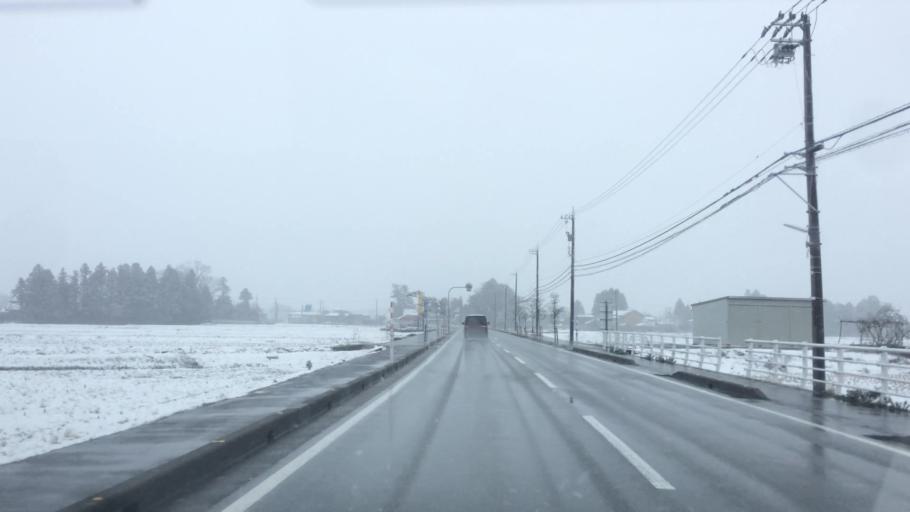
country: JP
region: Toyama
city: Toyama-shi
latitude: 36.6297
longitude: 137.2255
